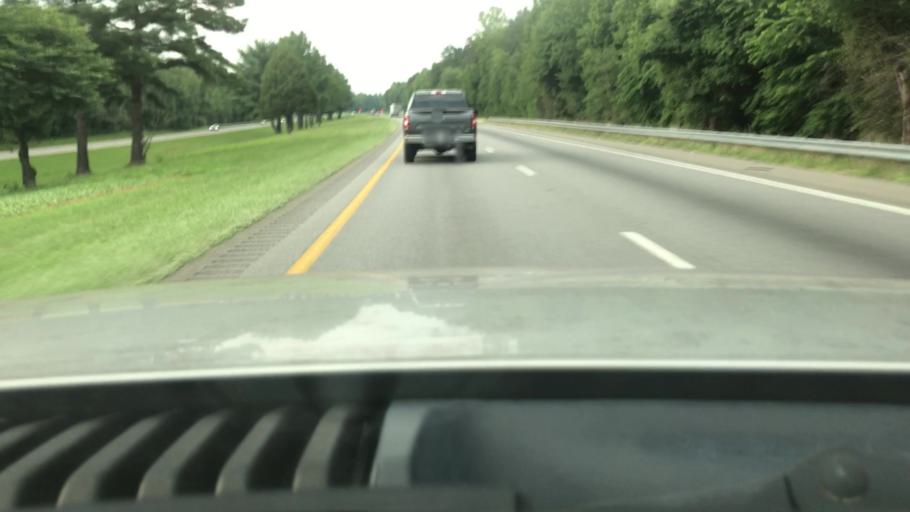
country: US
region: North Carolina
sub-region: Surry County
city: Dobson
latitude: 36.3474
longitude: -80.7952
